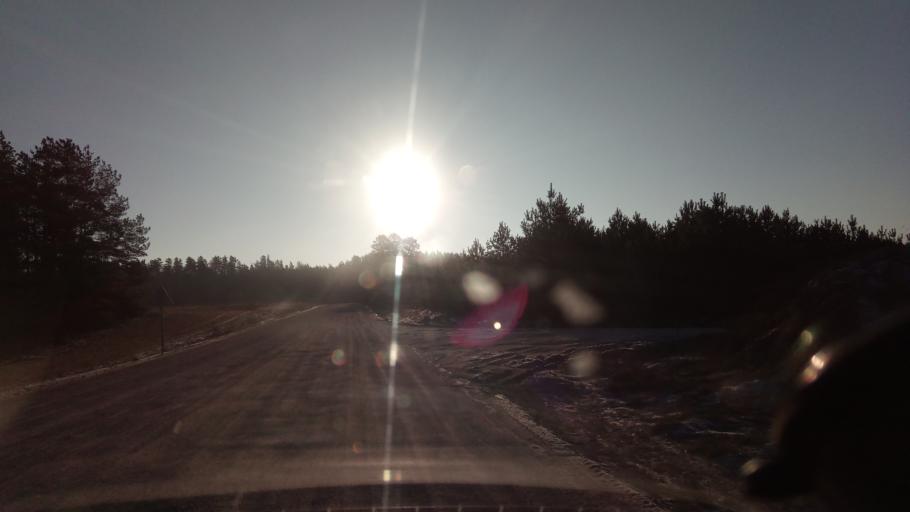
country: LT
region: Alytaus apskritis
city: Druskininkai
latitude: 54.1501
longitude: 23.9345
